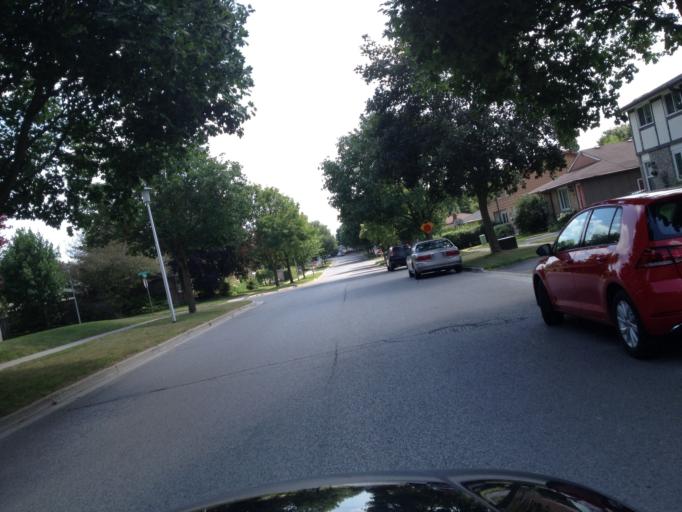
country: CA
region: Ontario
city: London
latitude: 43.0132
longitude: -81.3214
